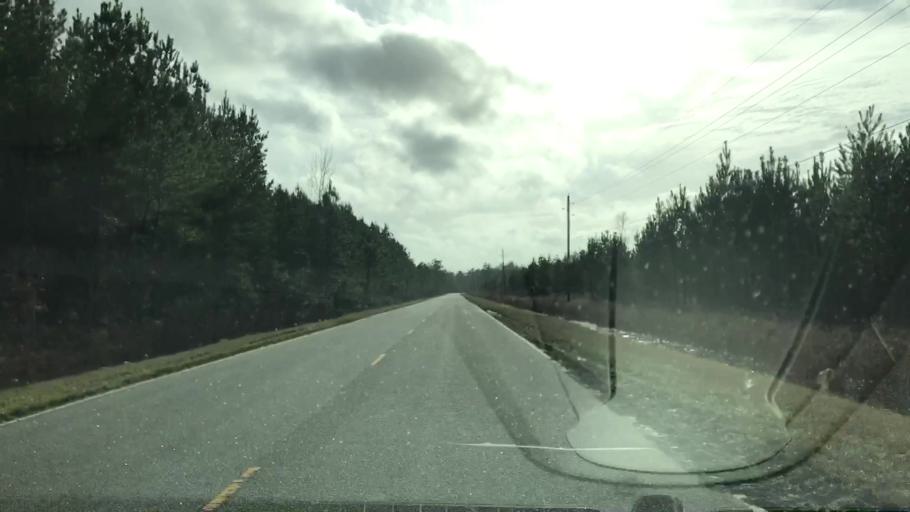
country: US
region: South Carolina
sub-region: Williamsburg County
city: Andrews
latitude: 33.4127
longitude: -79.6064
